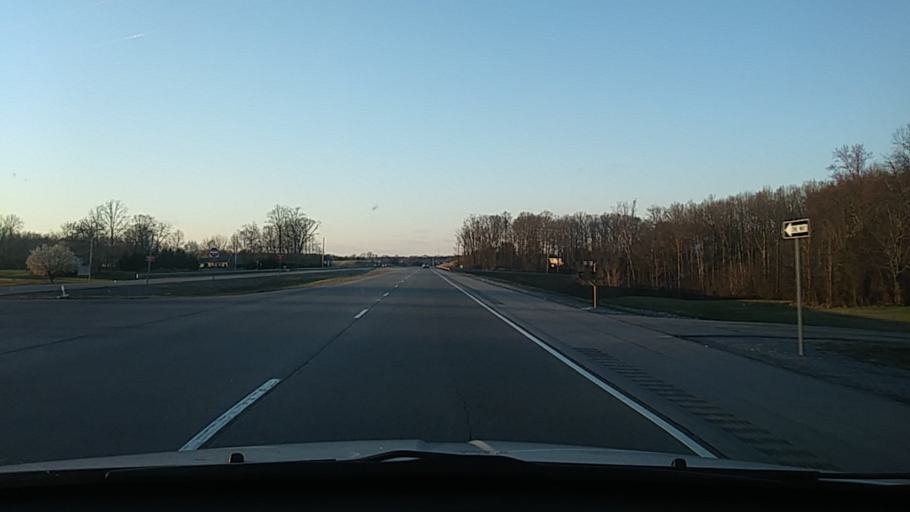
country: US
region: Tennessee
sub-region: Sumner County
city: Portland
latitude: 36.5142
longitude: -86.5063
